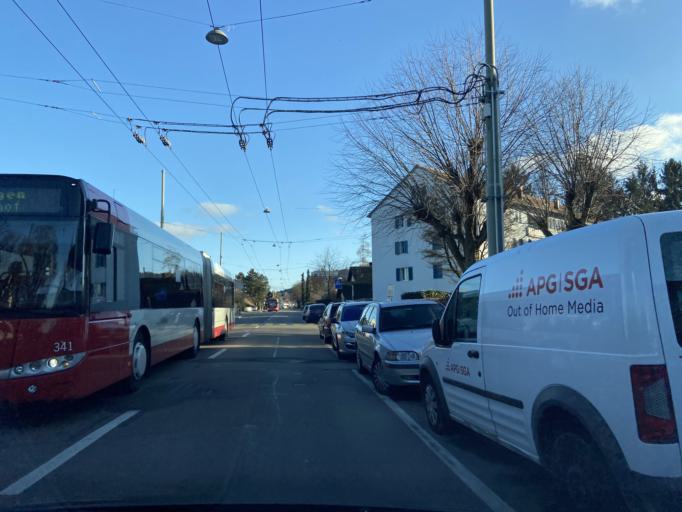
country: CH
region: Zurich
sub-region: Bezirk Winterthur
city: Wuelflingen (Kreis 6) / Haerti
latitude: 47.5128
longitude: 8.6872
